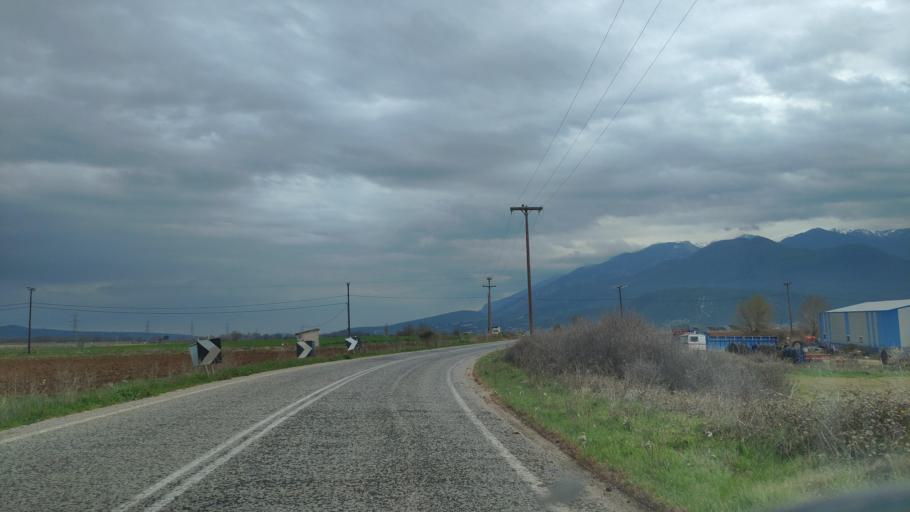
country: GR
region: Central Greece
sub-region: Nomos Fthiotidos
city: Amfikleia
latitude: 38.6934
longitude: 22.5275
